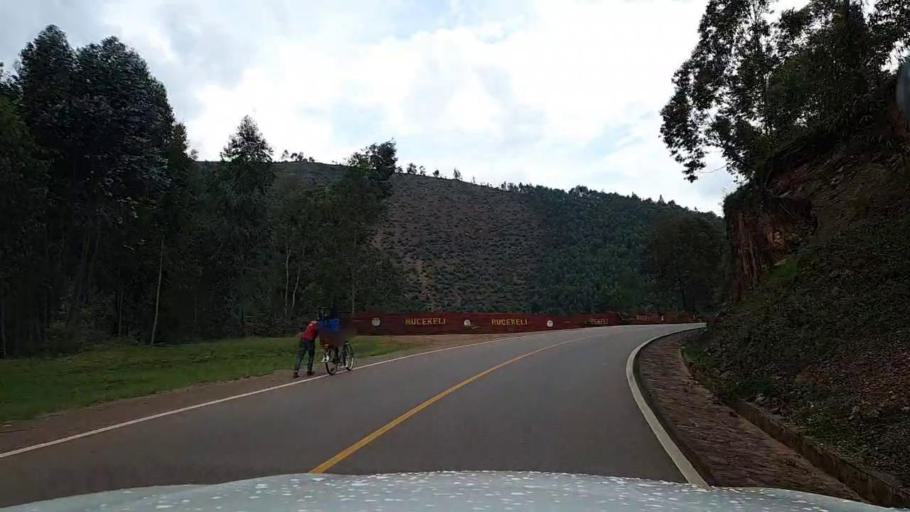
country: RW
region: Northern Province
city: Byumba
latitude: -1.7194
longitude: 30.1189
